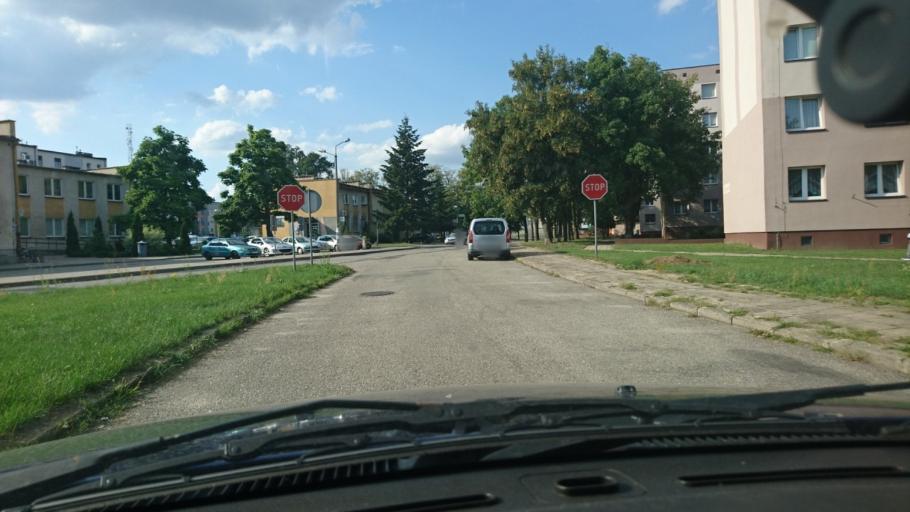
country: PL
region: Greater Poland Voivodeship
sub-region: Powiat ostrowski
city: Odolanow
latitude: 51.5782
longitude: 17.6605
